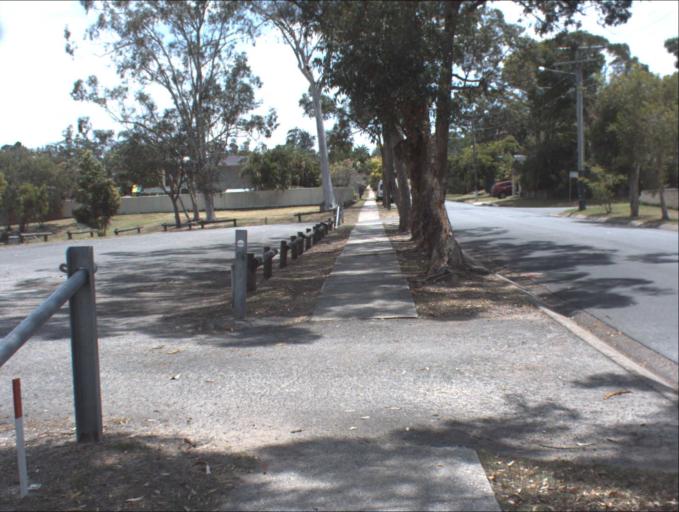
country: AU
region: Queensland
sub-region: Logan
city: Springwood
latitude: -27.6201
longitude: 153.1363
